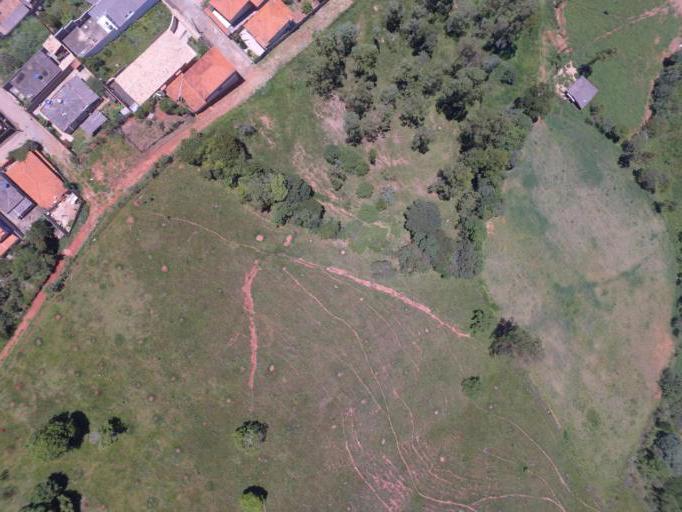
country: BR
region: Minas Gerais
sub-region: Tiradentes
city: Tiradentes
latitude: -21.0640
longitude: -44.0770
